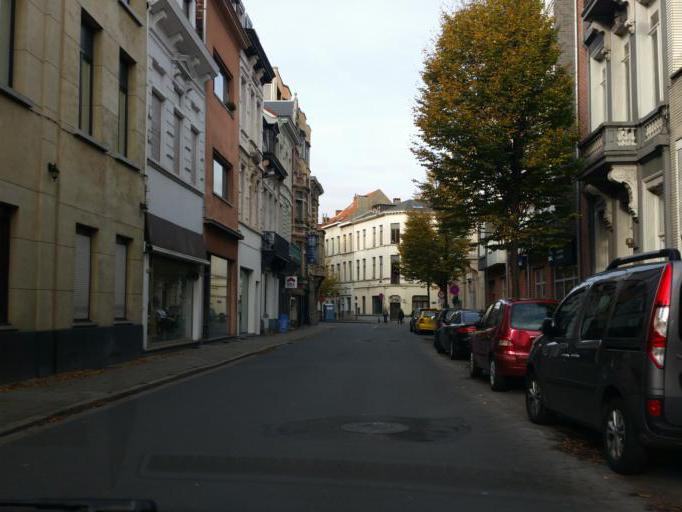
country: BE
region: Flanders
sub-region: Provincie Antwerpen
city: Antwerpen
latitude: 51.2051
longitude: 4.4044
